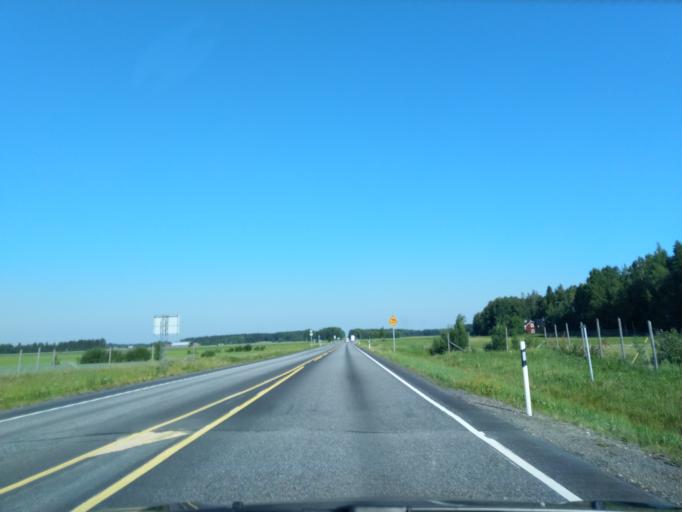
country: FI
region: Varsinais-Suomi
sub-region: Loimaa
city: Alastaro
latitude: 61.0602
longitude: 22.9409
